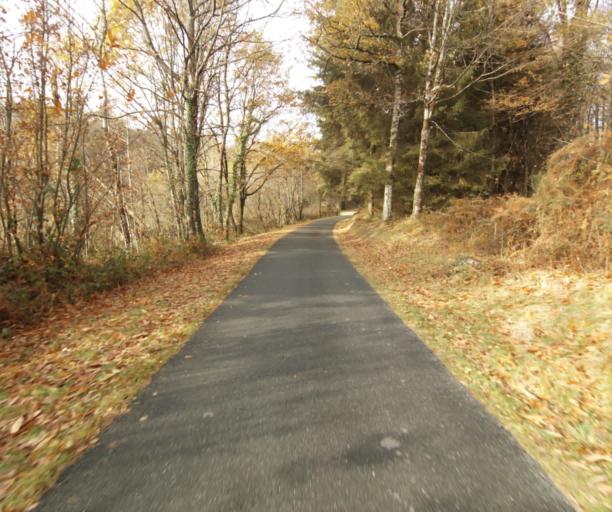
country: FR
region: Limousin
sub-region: Departement de la Correze
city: Sainte-Fortunade
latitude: 45.1795
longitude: 1.7479
